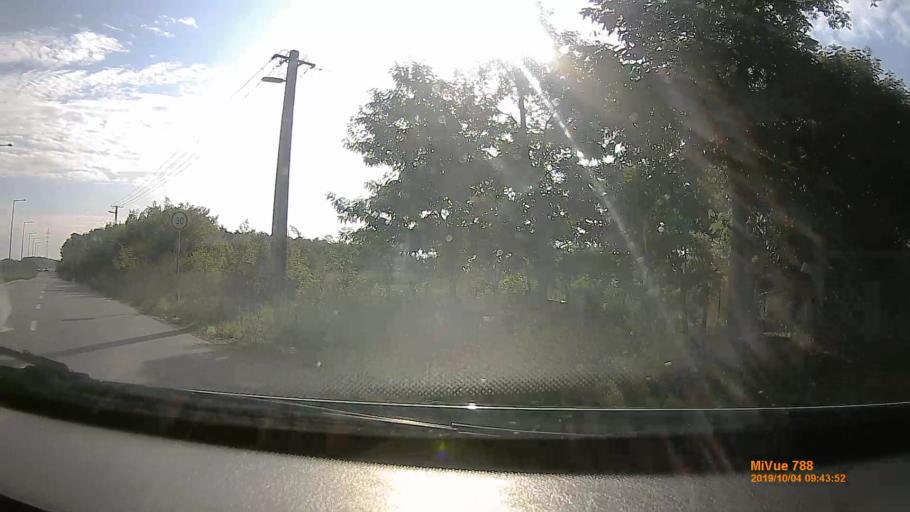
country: HU
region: Szabolcs-Szatmar-Bereg
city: Nyiregyhaza
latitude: 47.9446
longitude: 21.6492
